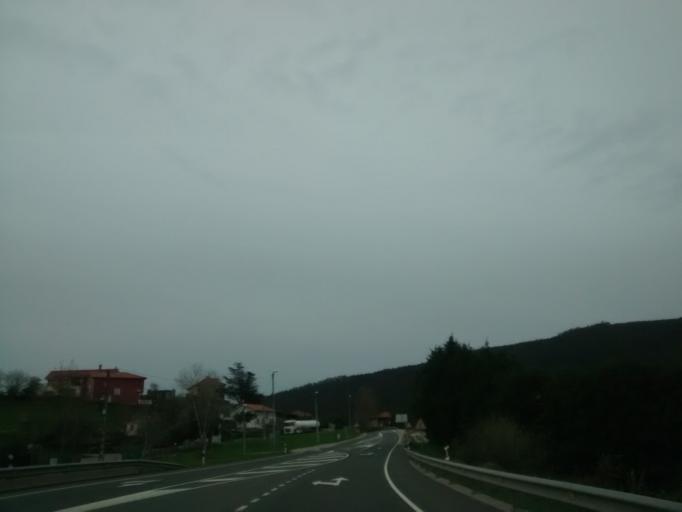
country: ES
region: Cantabria
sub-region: Provincia de Cantabria
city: Puente Viesgo
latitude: 43.3187
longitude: -3.9626
